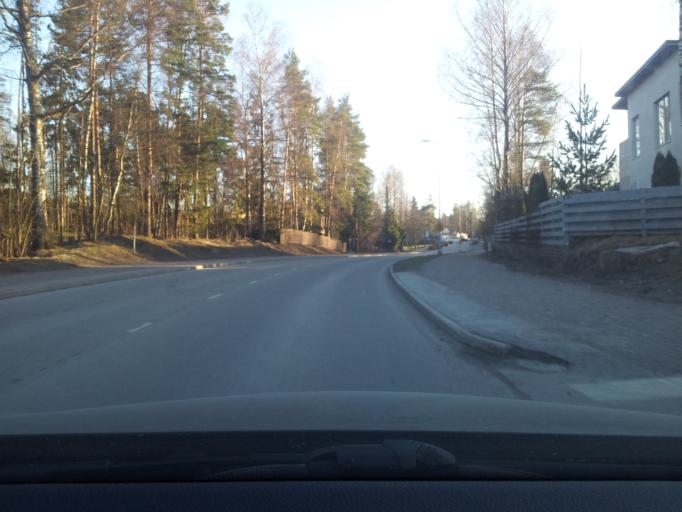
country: FI
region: Uusimaa
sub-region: Helsinki
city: Otaniemi
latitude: 60.1675
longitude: 24.8065
